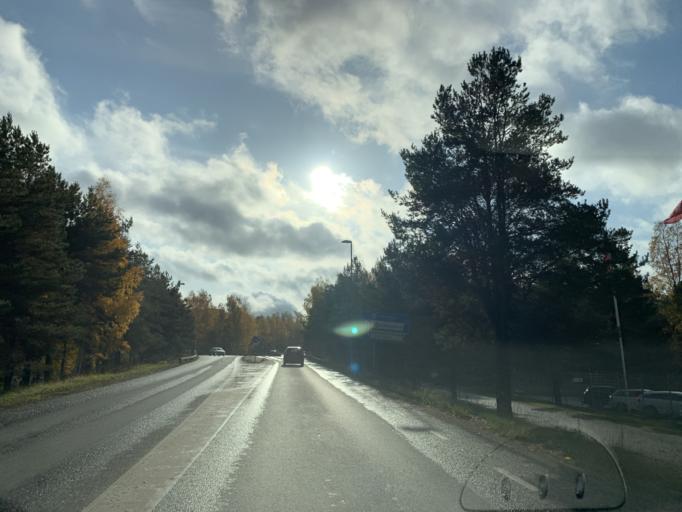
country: SE
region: Stockholm
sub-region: Haninge Kommun
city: Haninge
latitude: 59.1742
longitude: 18.1614
